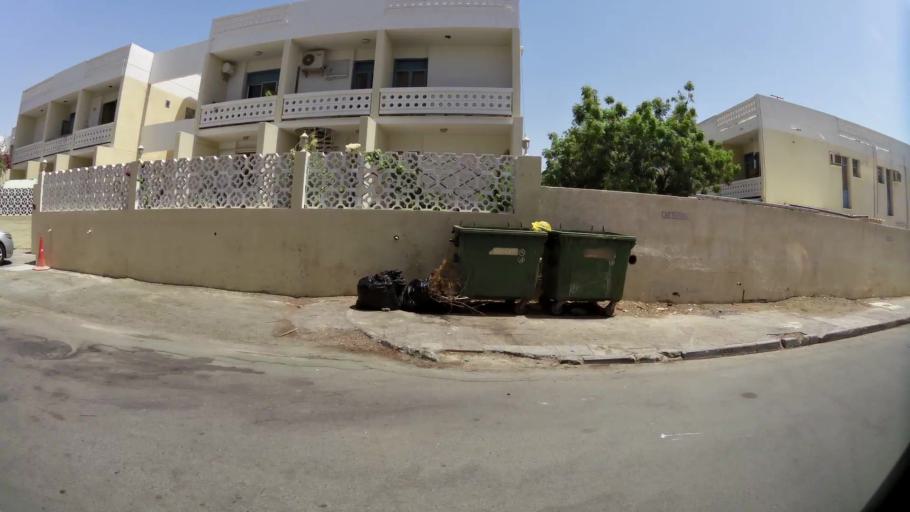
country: OM
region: Muhafazat Masqat
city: Muscat
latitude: 23.6322
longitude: 58.4823
